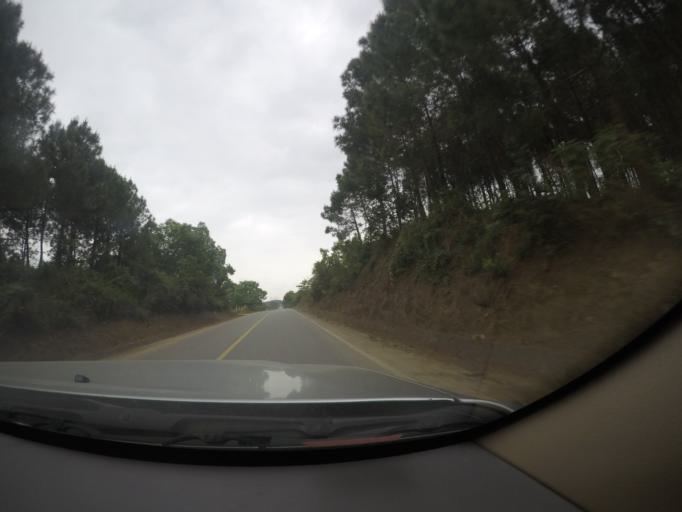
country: VN
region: Quang Binh
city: Ba Don
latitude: 17.6146
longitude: 106.3946
